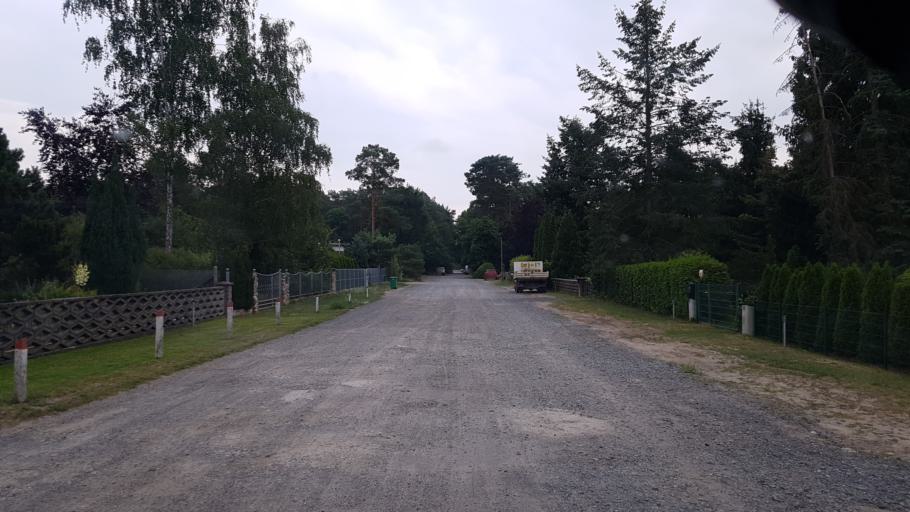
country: DE
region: Brandenburg
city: Gross Koris
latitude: 52.1640
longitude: 13.6947
